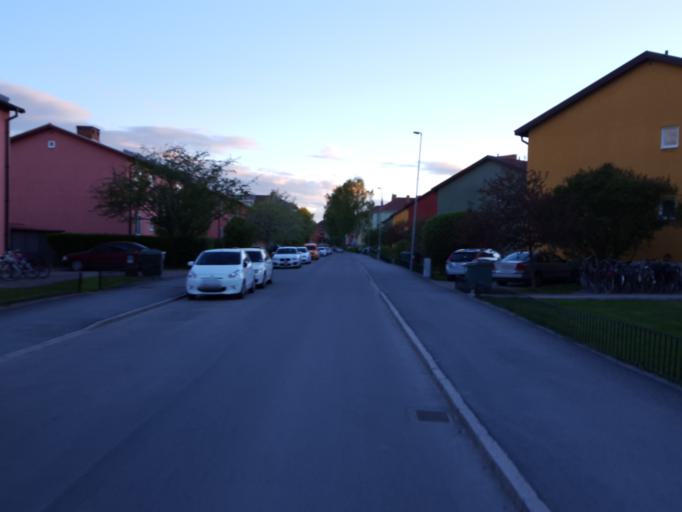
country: SE
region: Uppsala
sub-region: Uppsala Kommun
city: Uppsala
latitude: 59.8629
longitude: 17.6573
